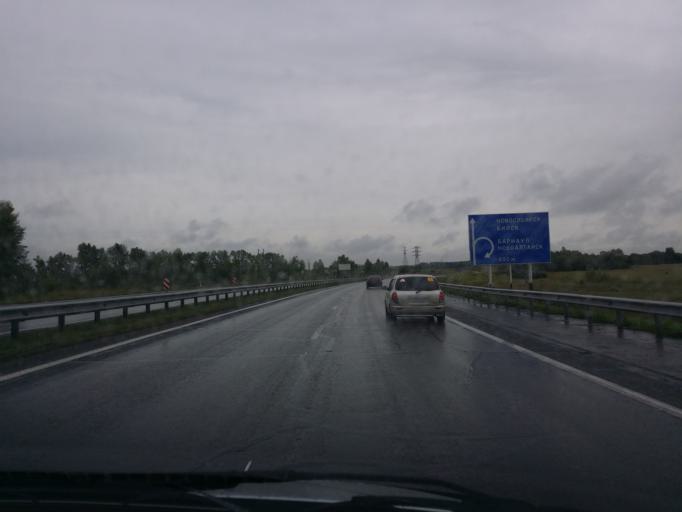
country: RU
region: Altai Krai
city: Novoaltaysk
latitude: 53.3653
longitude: 83.9475
